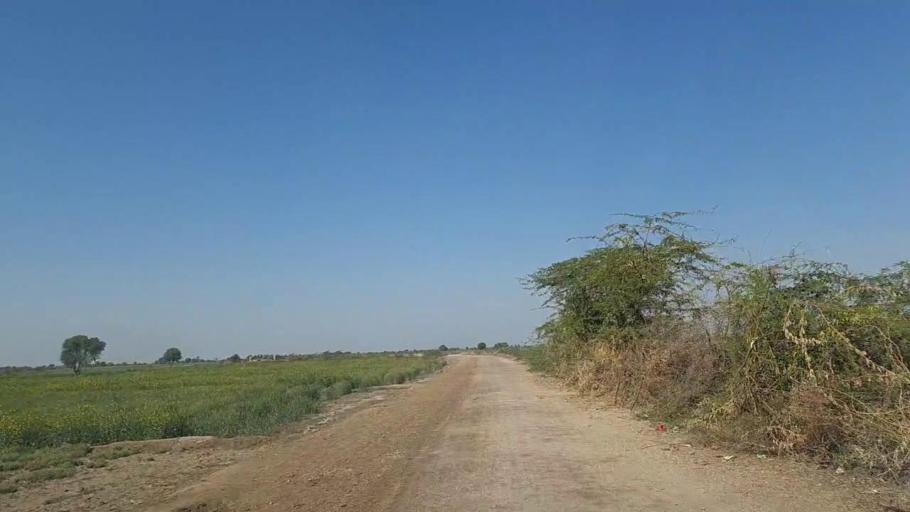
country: PK
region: Sindh
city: Naukot
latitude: 25.0184
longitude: 69.3590
